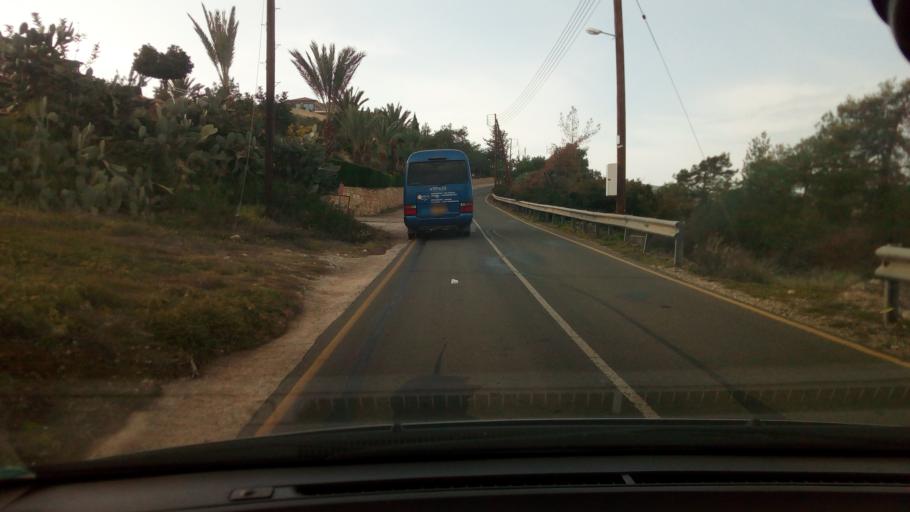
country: CY
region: Pafos
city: Polis
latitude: 35.0344
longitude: 32.3673
